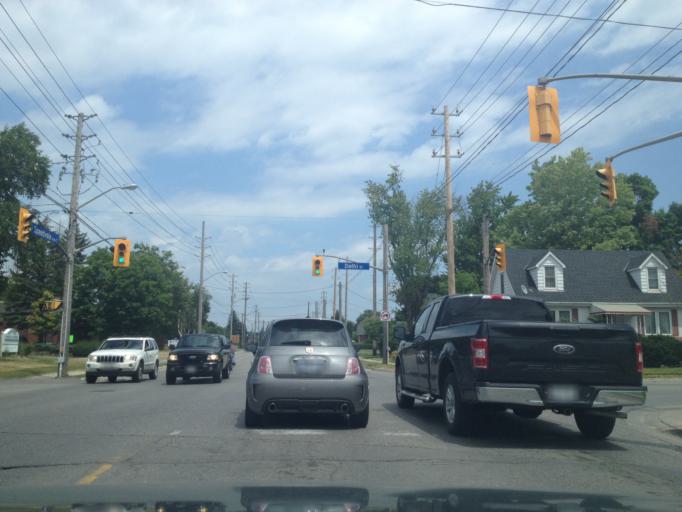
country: CA
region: Ontario
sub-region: Wellington County
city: Guelph
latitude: 43.5622
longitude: -80.2630
